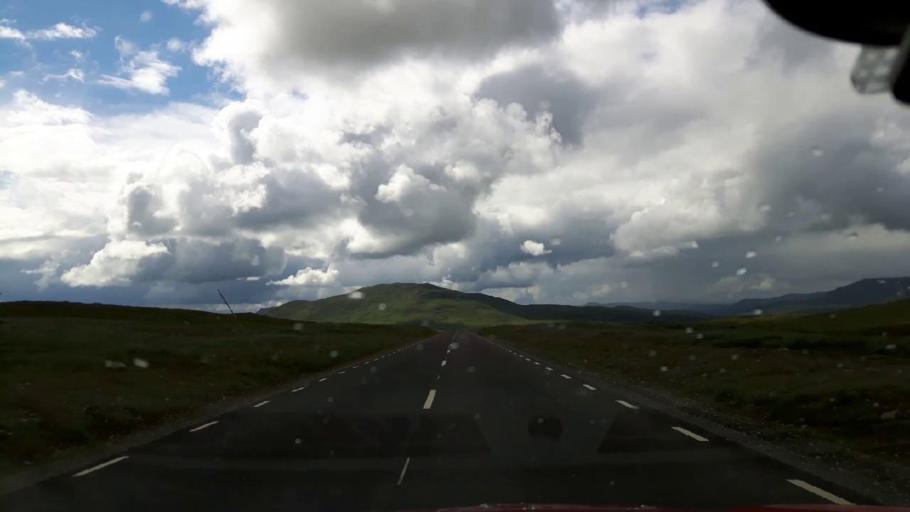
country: NO
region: Nordland
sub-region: Hattfjelldal
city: Hattfjelldal
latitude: 65.0430
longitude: 14.3300
